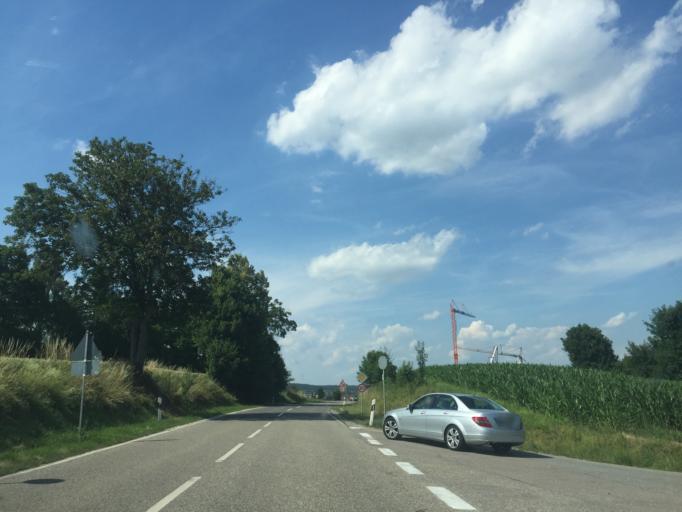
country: DE
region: Baden-Wuerttemberg
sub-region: Karlsruhe Region
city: Sinsheim
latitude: 49.2416
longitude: 8.8759
